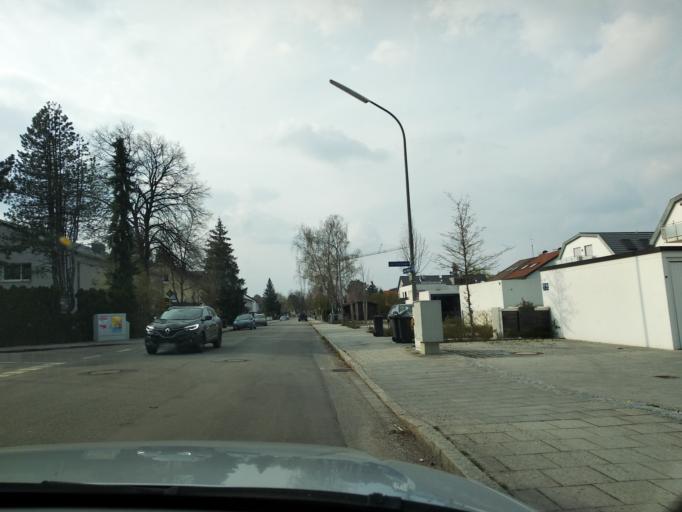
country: DE
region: Bavaria
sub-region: Upper Bavaria
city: Vaterstetten
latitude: 48.1068
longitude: 11.7807
